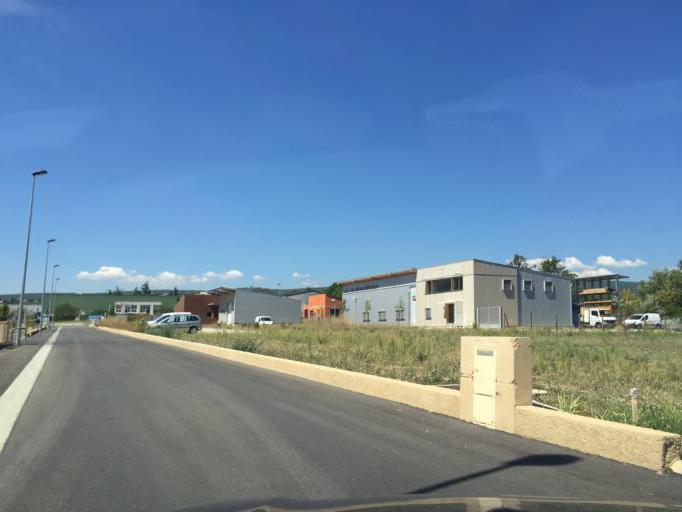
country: FR
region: Provence-Alpes-Cote d'Azur
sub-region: Departement des Alpes-de-Haute-Provence
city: Forcalquier
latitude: 43.9566
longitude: 5.8031
